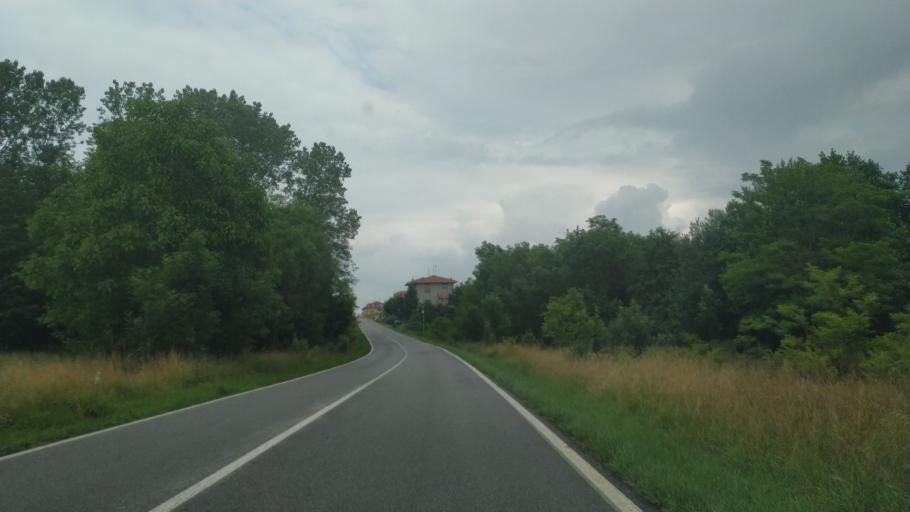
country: IT
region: Piedmont
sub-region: Provincia di Novara
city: Cavallirio
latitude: 45.6581
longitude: 8.3870
